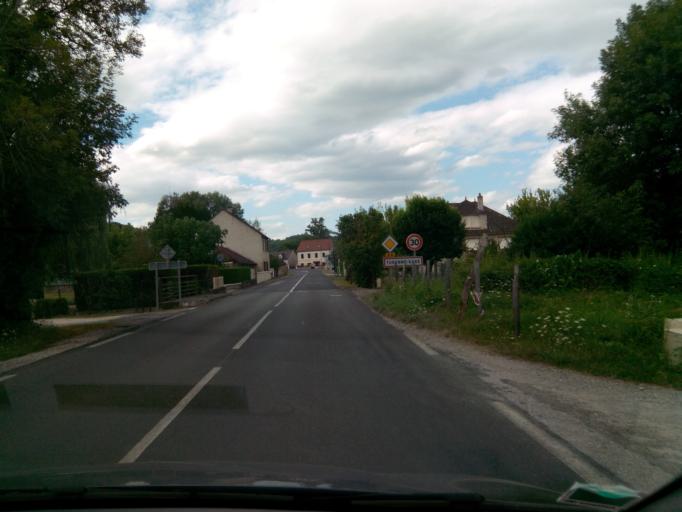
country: FR
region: Limousin
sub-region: Departement de la Correze
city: Meyssac
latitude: 45.0349
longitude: 1.6038
